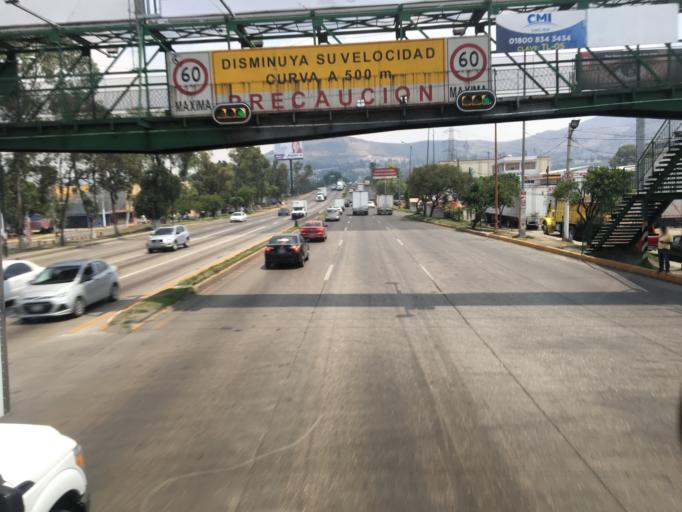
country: MX
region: Mexico
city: Tlalnepantla
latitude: 19.5506
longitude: -99.1840
